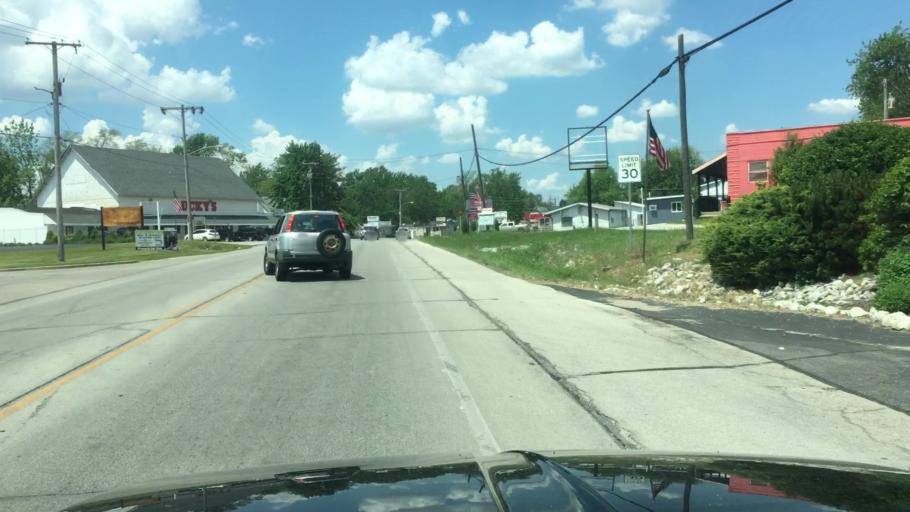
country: US
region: Indiana
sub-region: Kosciusko County
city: North Webster
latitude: 41.3210
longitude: -85.6966
